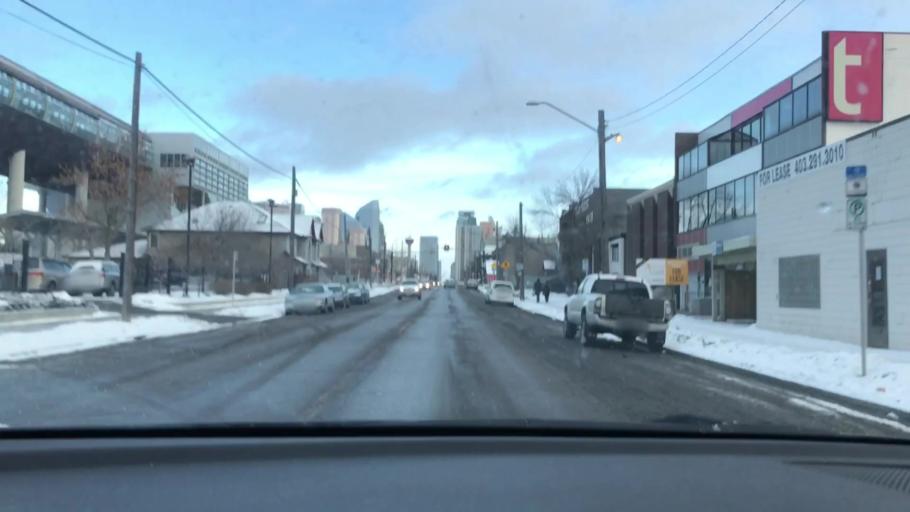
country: CA
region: Alberta
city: Calgary
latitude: 51.0444
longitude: -114.1014
